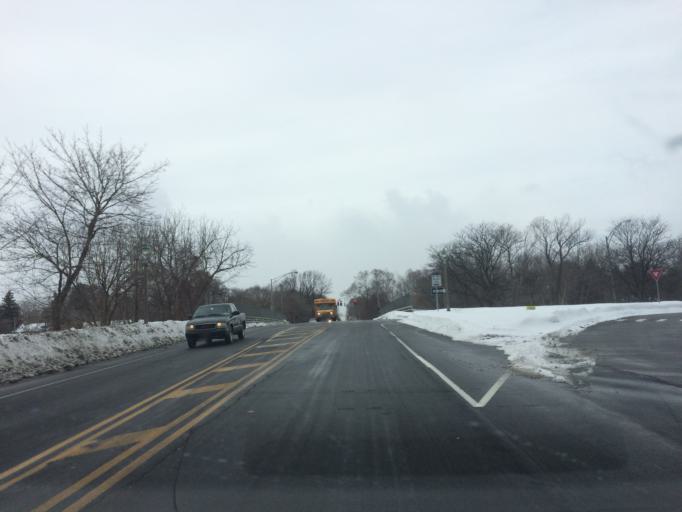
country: US
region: New York
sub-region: Monroe County
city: Brighton
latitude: 43.1269
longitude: -77.5522
